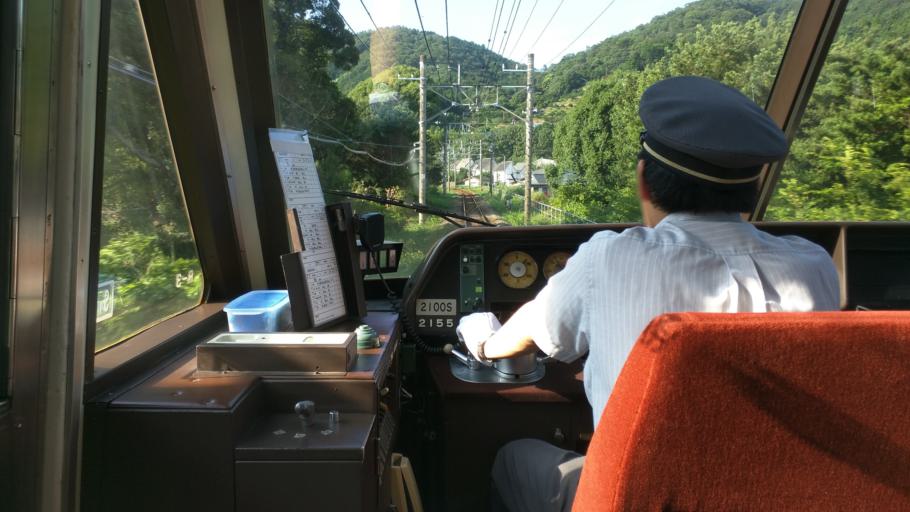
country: JP
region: Shizuoka
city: Atami
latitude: 35.0666
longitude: 139.0669
